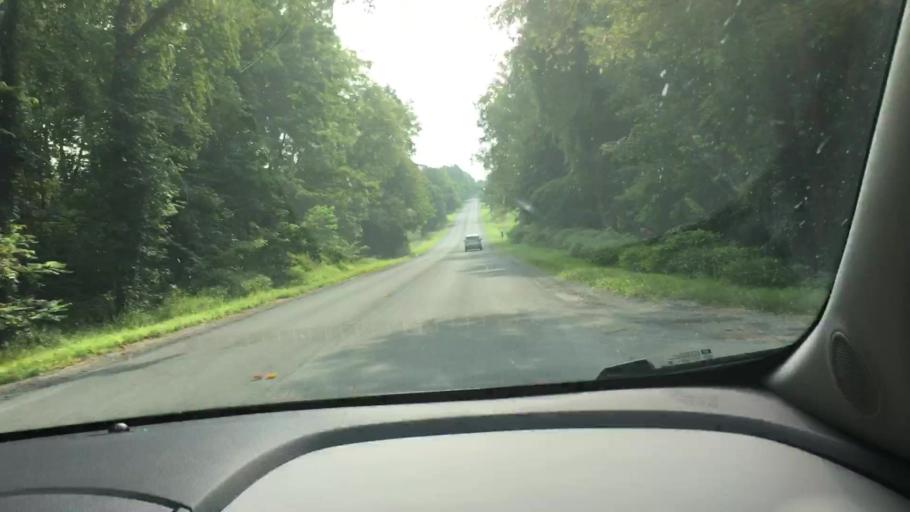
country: US
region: Michigan
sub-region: Kalamazoo County
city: Schoolcraft
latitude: 42.0273
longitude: -85.7035
